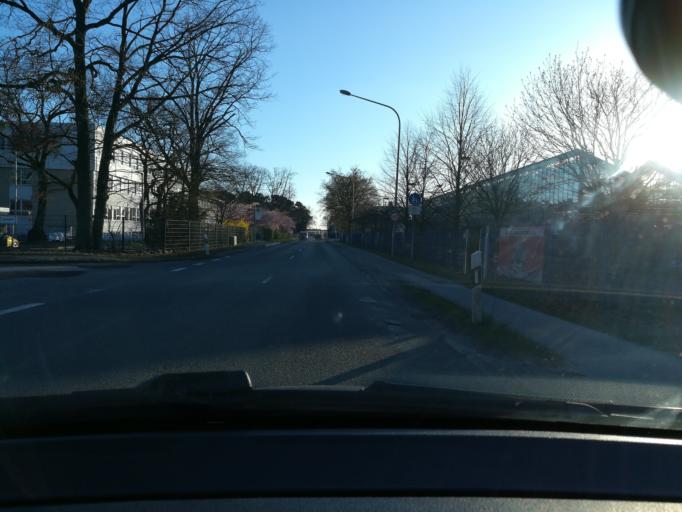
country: DE
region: North Rhine-Westphalia
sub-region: Regierungsbezirk Detmold
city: Oerlinghausen
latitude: 51.9567
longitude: 8.5821
